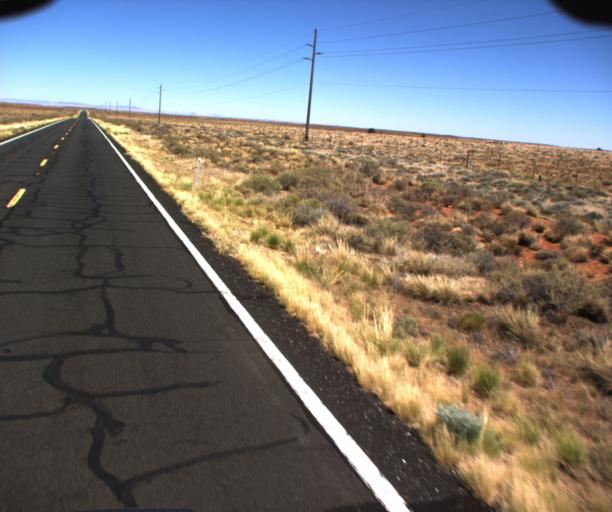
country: US
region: Arizona
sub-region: Coconino County
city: LeChee
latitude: 34.8935
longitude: -110.8643
